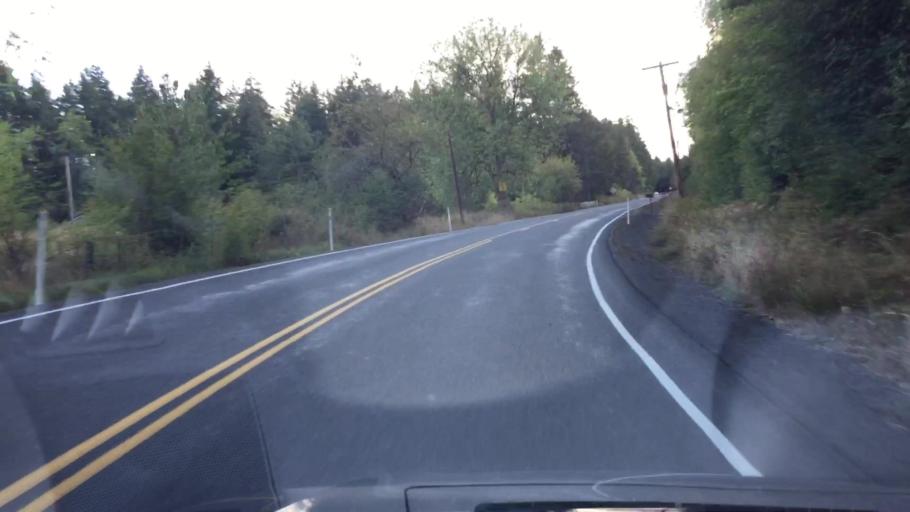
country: US
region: Washington
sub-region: Lewis County
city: Napavine
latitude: 46.5099
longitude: -122.7491
